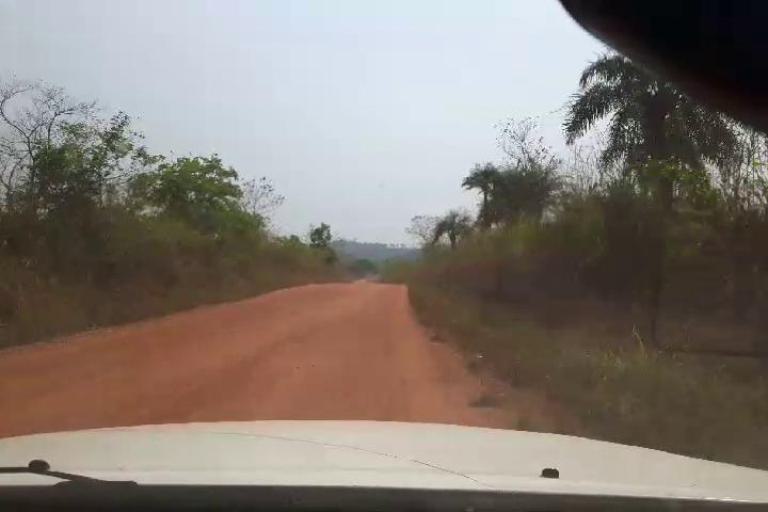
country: SL
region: Northern Province
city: Bumbuna
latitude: 8.9444
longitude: -11.8139
